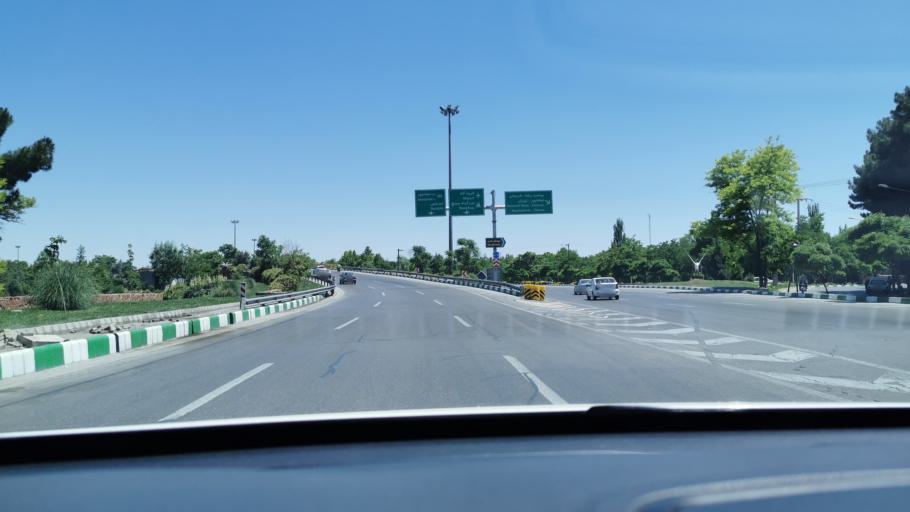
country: IR
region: Razavi Khorasan
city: Mashhad
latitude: 36.2506
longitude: 59.6073
